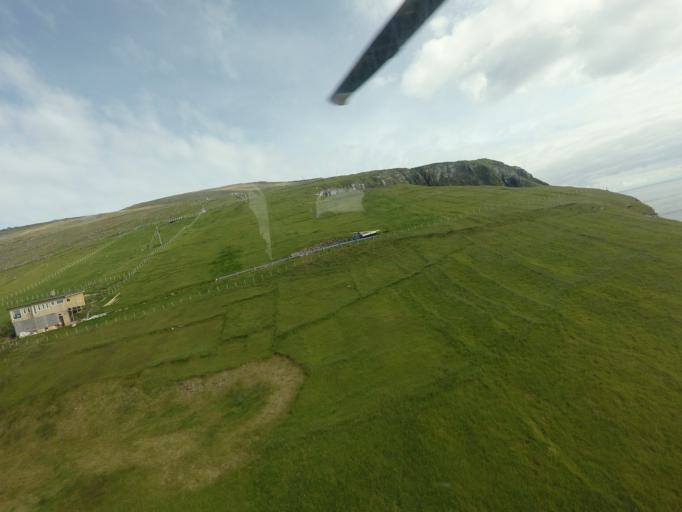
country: FO
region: Nordoyar
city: Klaksvik
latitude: 62.3169
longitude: -6.3126
